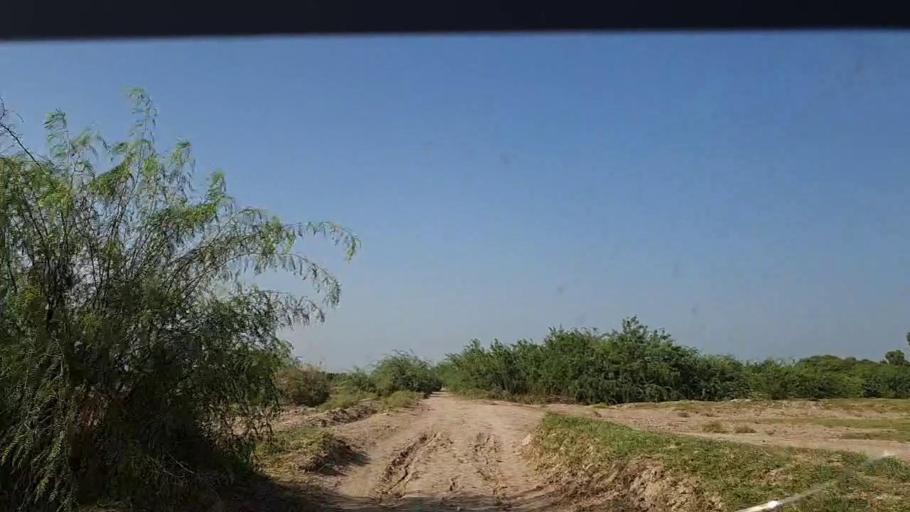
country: PK
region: Sindh
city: Adilpur
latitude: 27.9047
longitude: 69.2266
